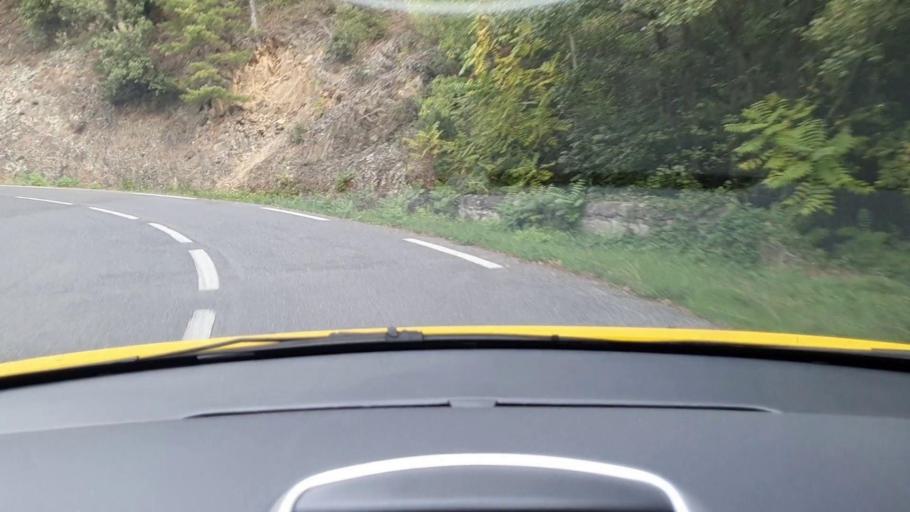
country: FR
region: Languedoc-Roussillon
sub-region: Departement du Gard
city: Le Vigan
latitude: 44.0105
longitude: 3.5957
